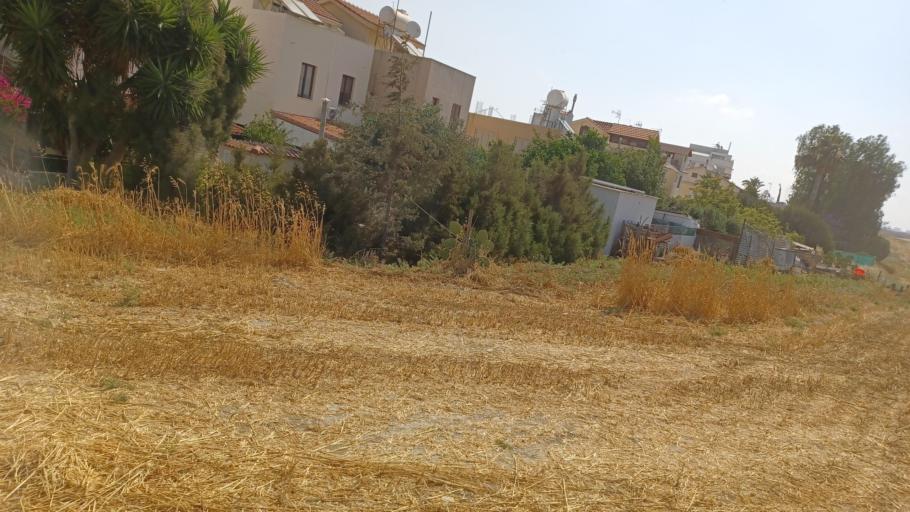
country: CY
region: Larnaka
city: Dhromolaxia
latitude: 34.9023
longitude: 33.5861
